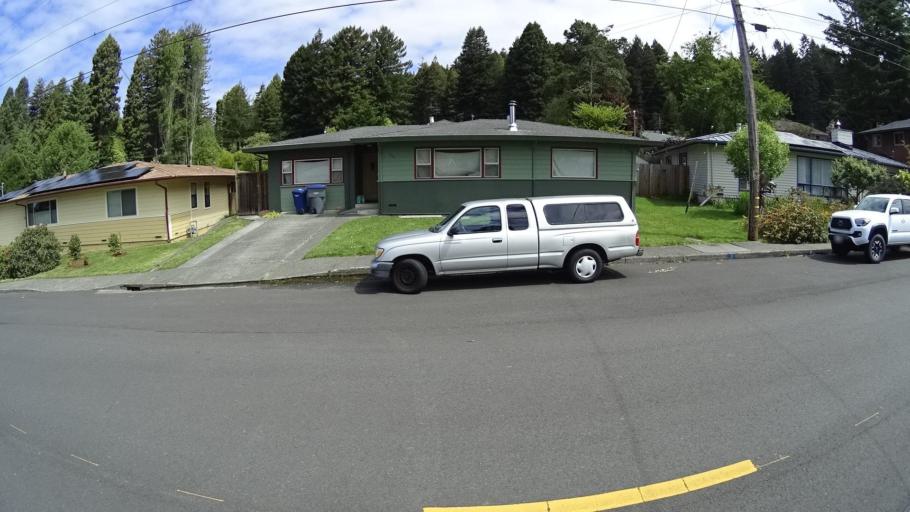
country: US
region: California
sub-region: Humboldt County
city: Bayside
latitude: 40.8583
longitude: -124.0627
